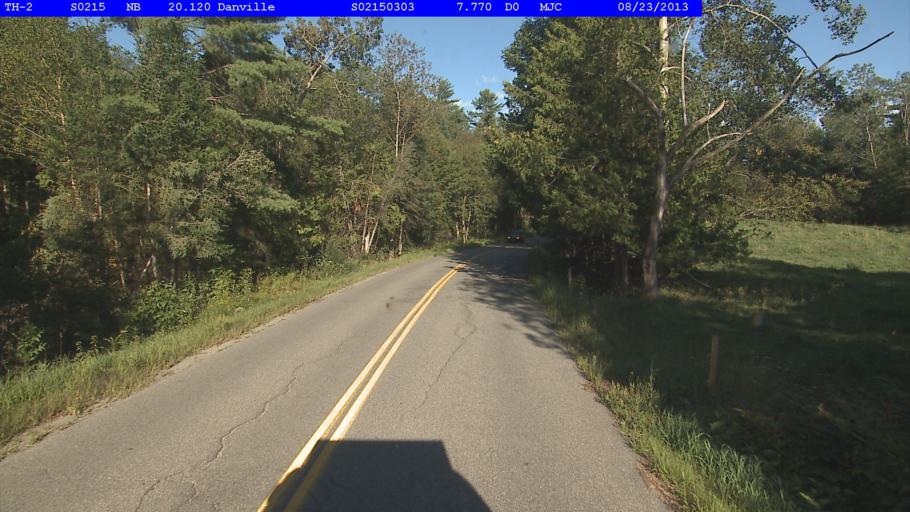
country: US
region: Vermont
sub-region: Caledonia County
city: St Johnsbury
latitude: 44.4585
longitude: -72.1051
